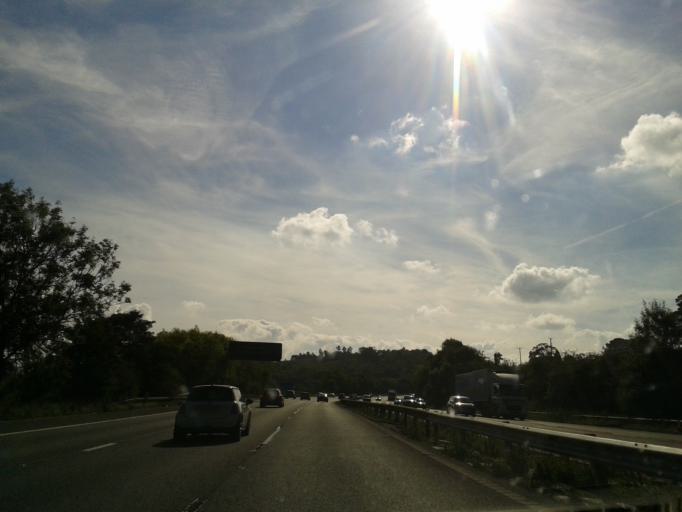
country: GB
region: England
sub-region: Staffordshire
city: Newcastle under Lyme
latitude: 52.9697
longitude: -2.2240
